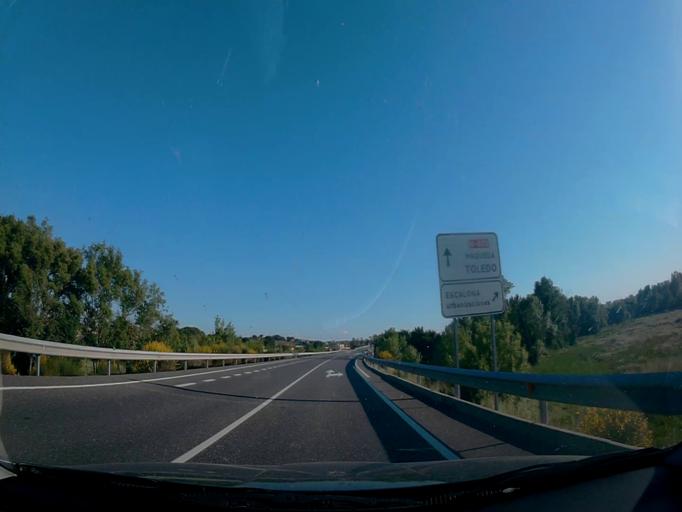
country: ES
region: Castille-La Mancha
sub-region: Province of Toledo
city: Escalona
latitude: 40.1634
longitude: -4.3982
